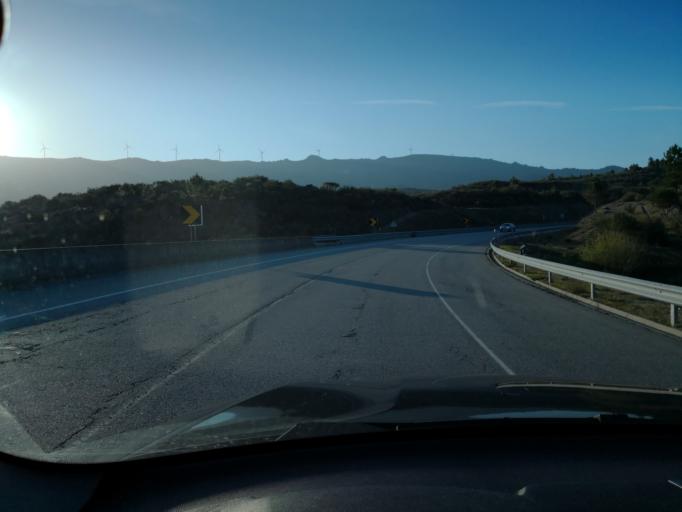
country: PT
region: Vila Real
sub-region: Vila Real
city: Vila Real
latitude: 41.3675
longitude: -7.7123
